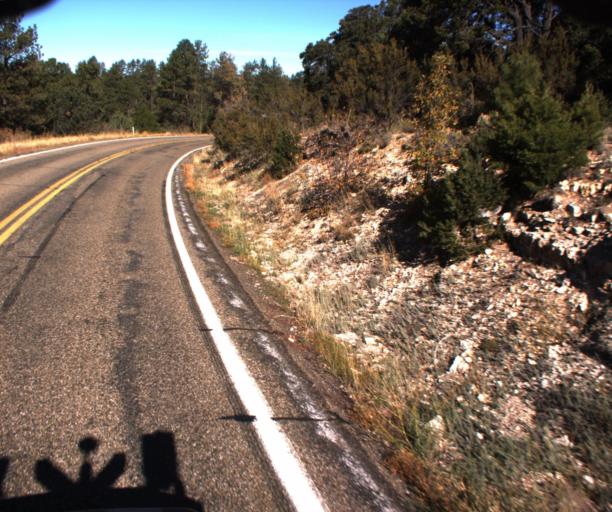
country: US
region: Arizona
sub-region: Coconino County
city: Fredonia
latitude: 36.7752
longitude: -112.2551
